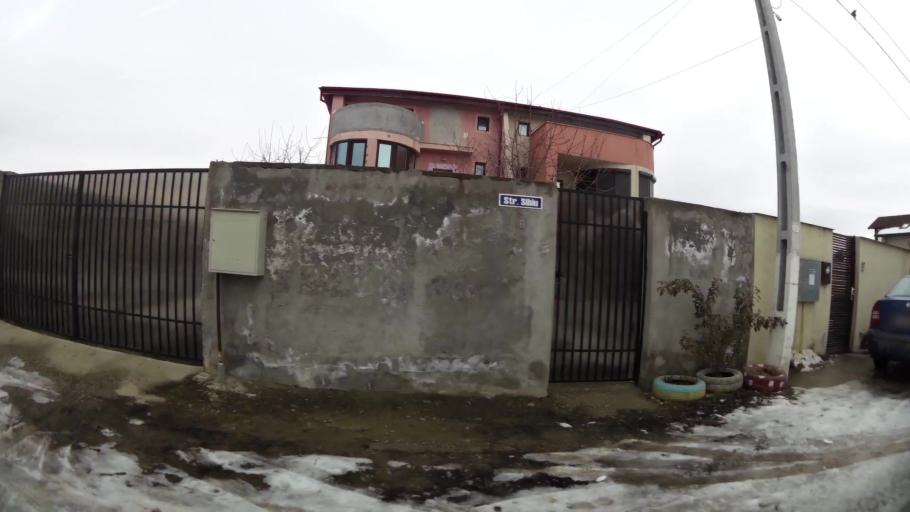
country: RO
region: Ilfov
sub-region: Comuna Pantelimon
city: Pantelimon
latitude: 44.4565
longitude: 26.2188
